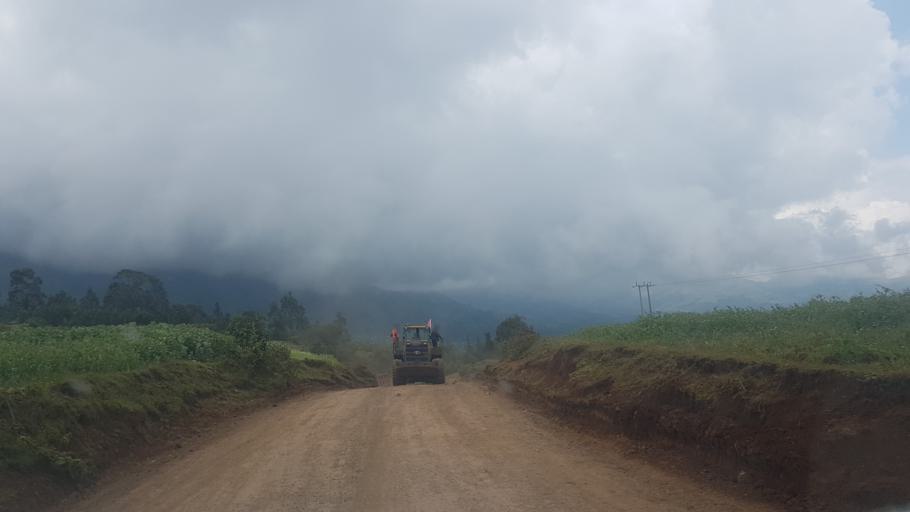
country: ET
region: Southern Nations, Nationalities, and People's Region
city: Arba Minch'
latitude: 6.3235
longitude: 37.5397
